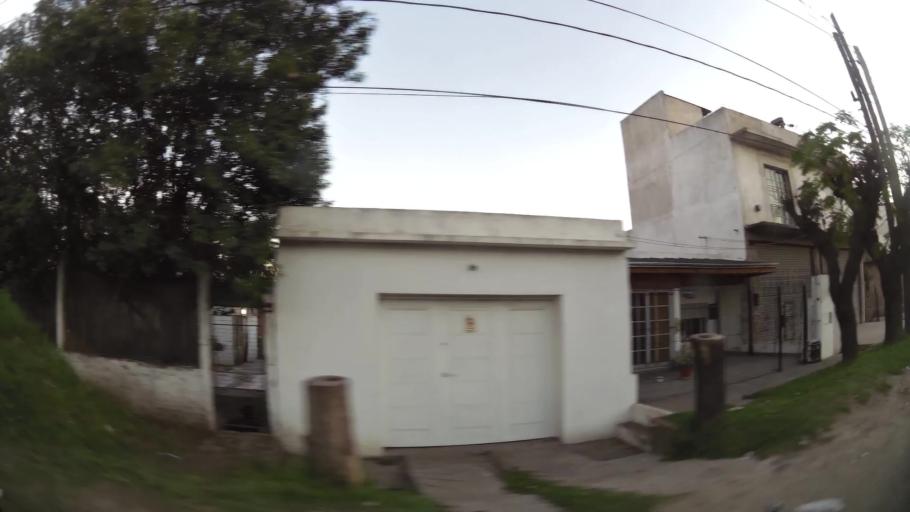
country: AR
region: Buenos Aires
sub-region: Partido de Almirante Brown
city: Adrogue
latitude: -34.7991
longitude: -58.3254
